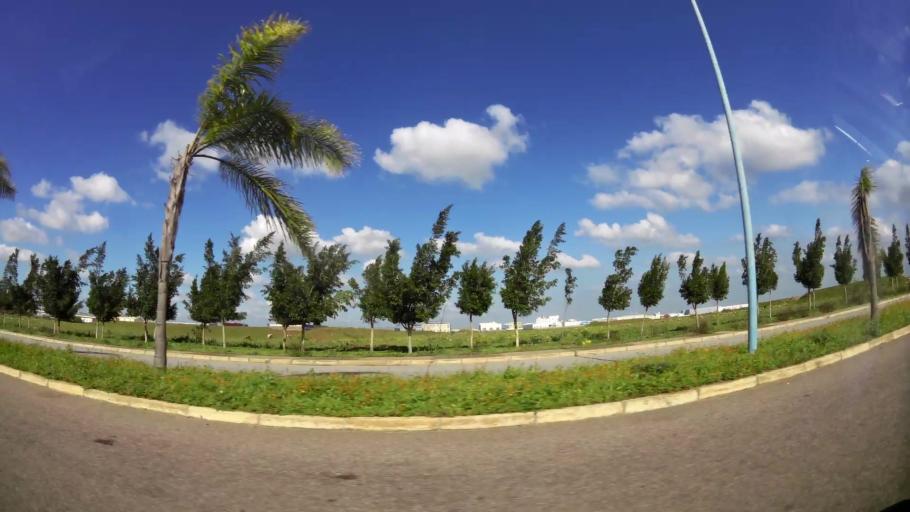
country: MA
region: Grand Casablanca
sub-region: Mediouna
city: Mediouna
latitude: 33.3989
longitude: -7.5548
